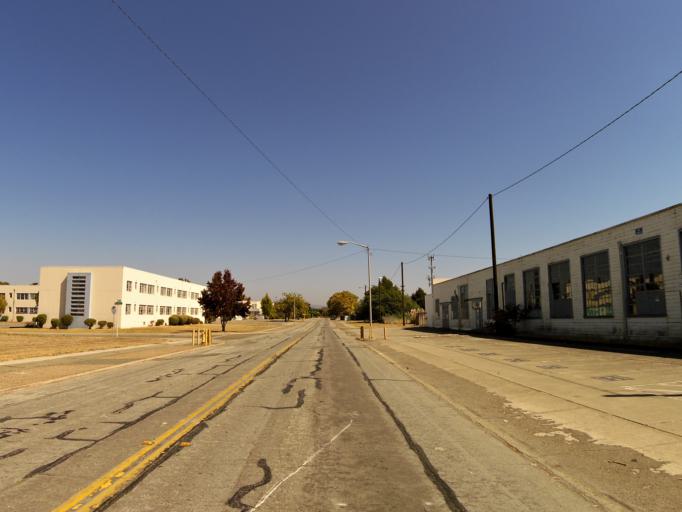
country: US
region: California
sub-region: Alameda County
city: Oakland
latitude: 37.7857
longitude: -122.3014
